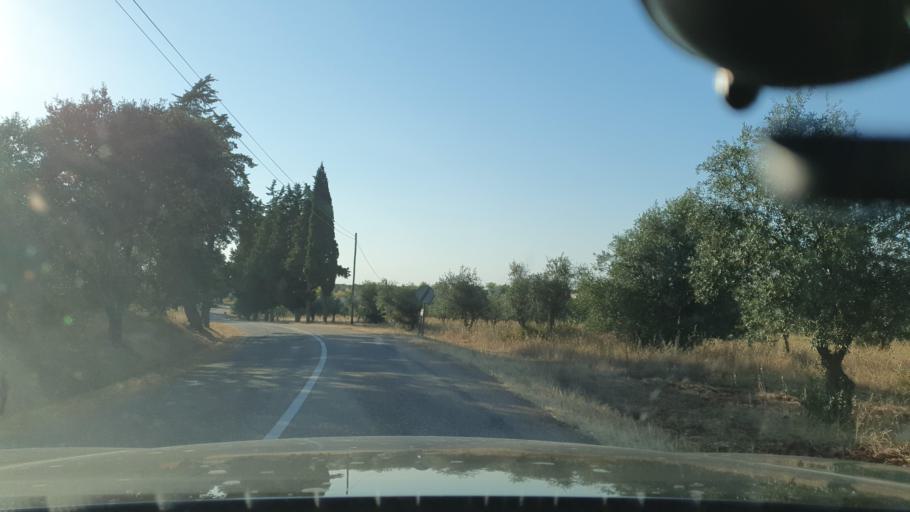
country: PT
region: Portalegre
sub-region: Fronteira
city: Fronteira
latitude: 38.9379
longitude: -7.6720
